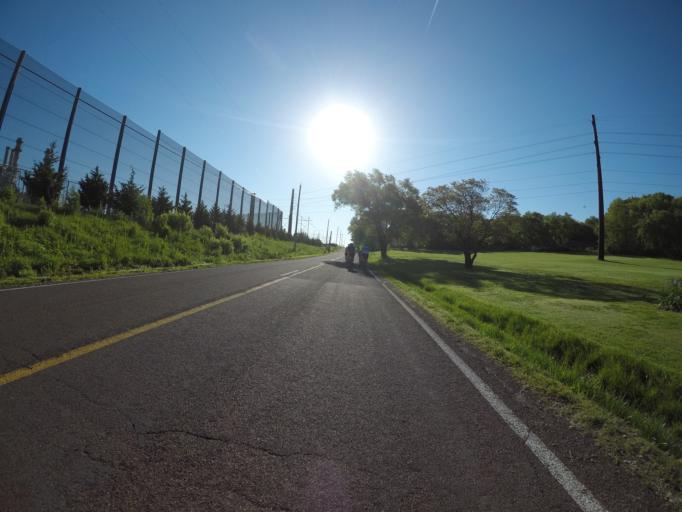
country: US
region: Kansas
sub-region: Shawnee County
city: Topeka
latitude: 39.0515
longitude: -95.5698
